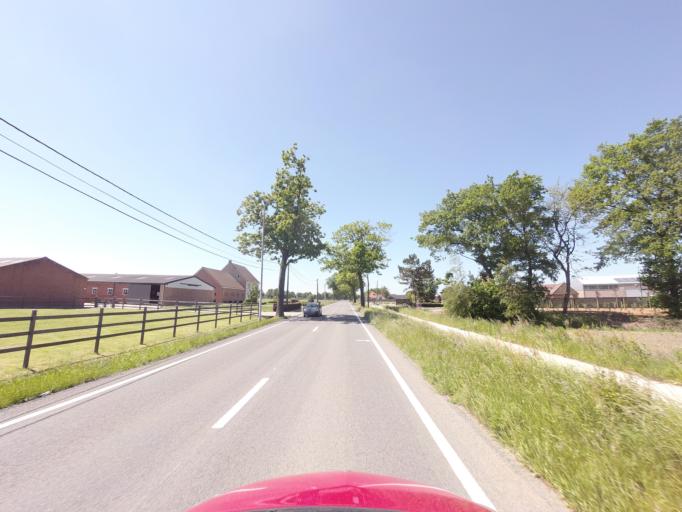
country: BE
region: Flanders
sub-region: Provincie Antwerpen
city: Ravels
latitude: 51.3806
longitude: 5.0257
